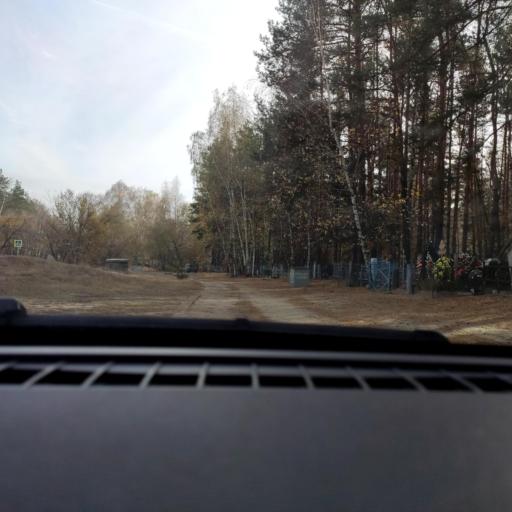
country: RU
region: Voronezj
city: Maslovka
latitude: 51.5776
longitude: 39.2945
